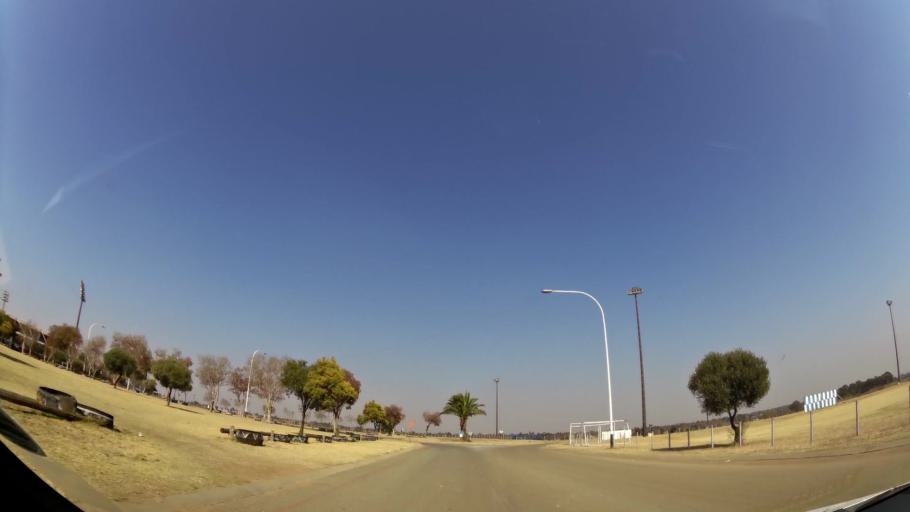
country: ZA
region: Gauteng
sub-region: Ekurhuleni Metropolitan Municipality
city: Boksburg
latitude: -26.2347
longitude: 28.2756
